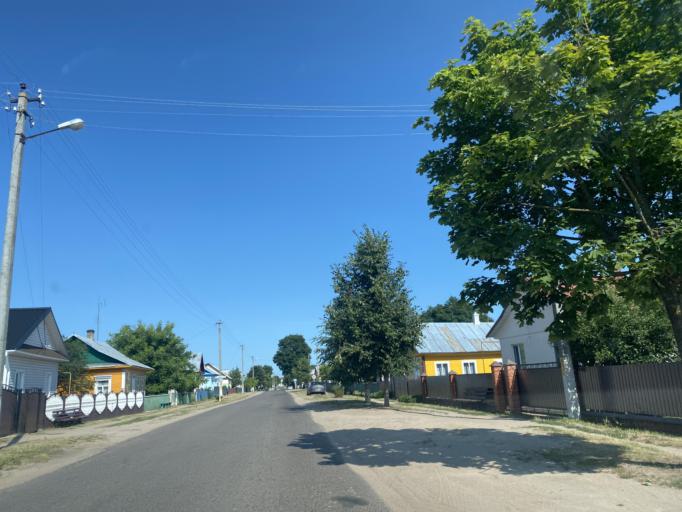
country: BY
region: Brest
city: Ivanava
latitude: 52.3136
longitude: 25.6155
